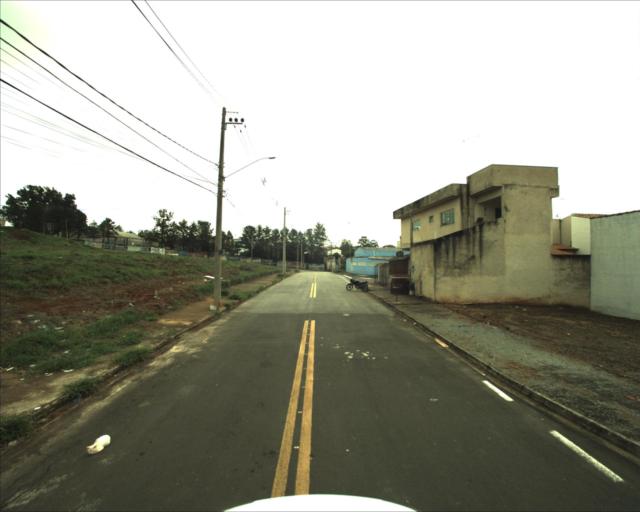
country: BR
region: Sao Paulo
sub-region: Sorocaba
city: Sorocaba
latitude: -23.4436
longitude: -47.4774
